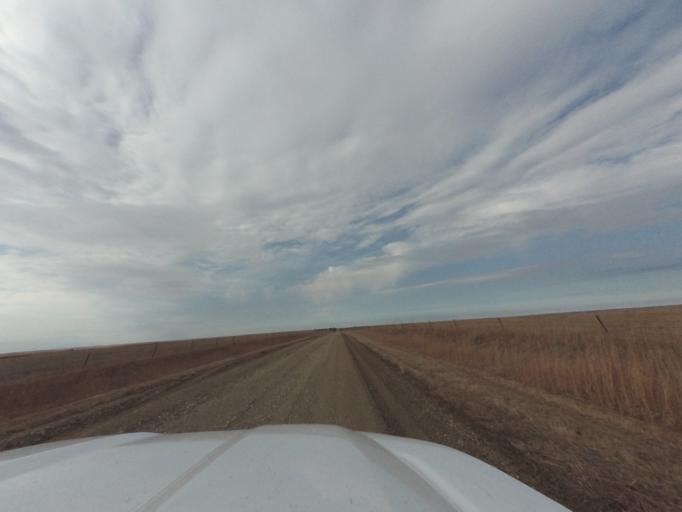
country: US
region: Kansas
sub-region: Chase County
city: Cottonwood Falls
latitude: 38.2171
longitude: -96.7197
